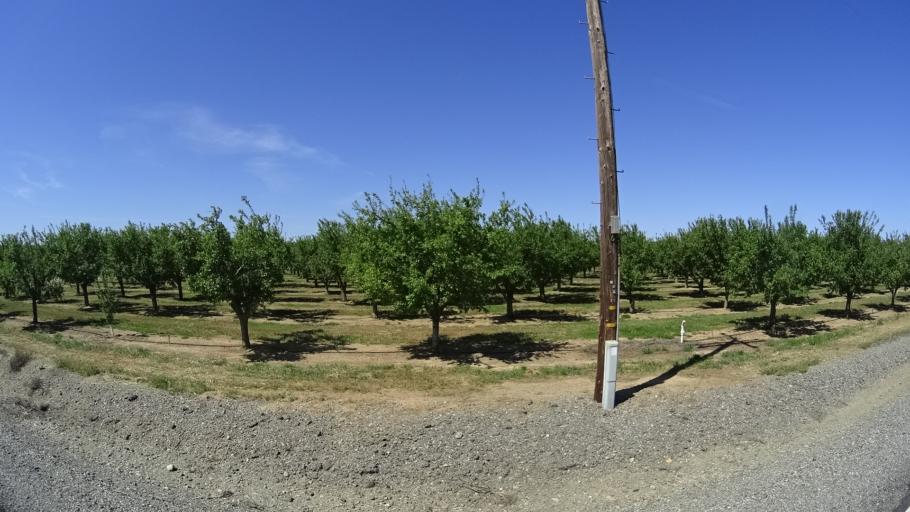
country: US
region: California
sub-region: Glenn County
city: Orland
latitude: 39.6752
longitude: -122.1405
